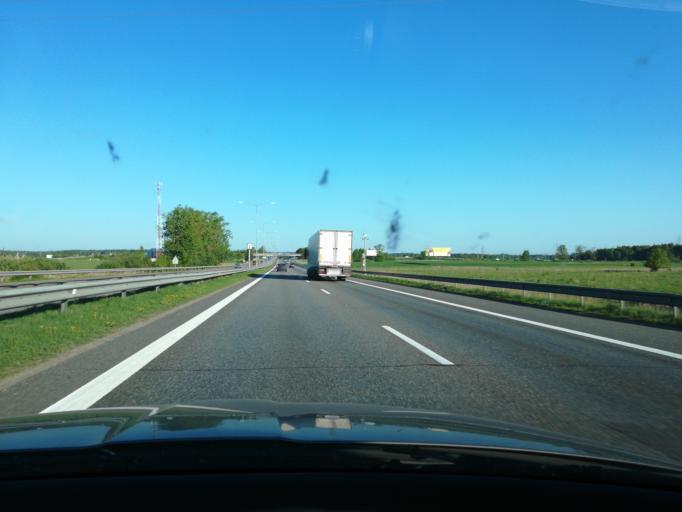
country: LT
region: Kauno apskritis
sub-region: Kauno rajonas
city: Karmelava
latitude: 54.8740
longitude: 24.2256
